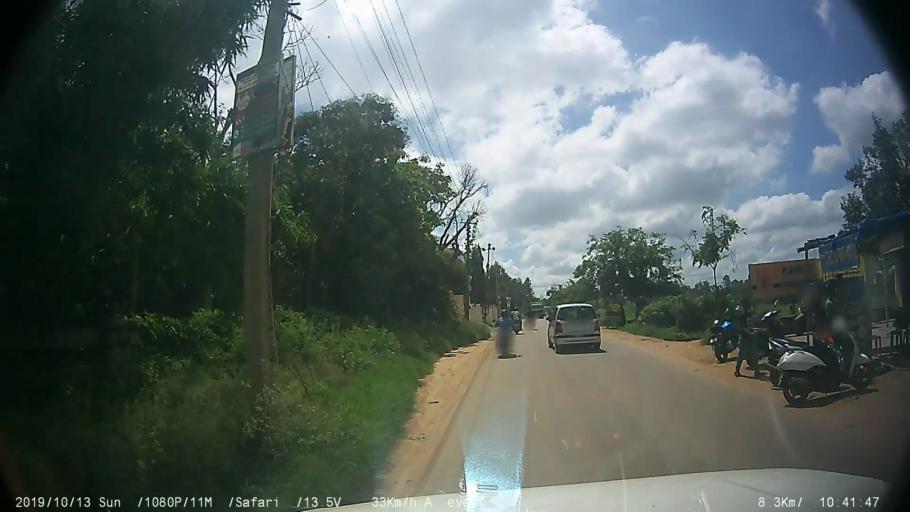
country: IN
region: Karnataka
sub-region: Bangalore Urban
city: Anekal
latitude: 12.8250
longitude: 77.6503
